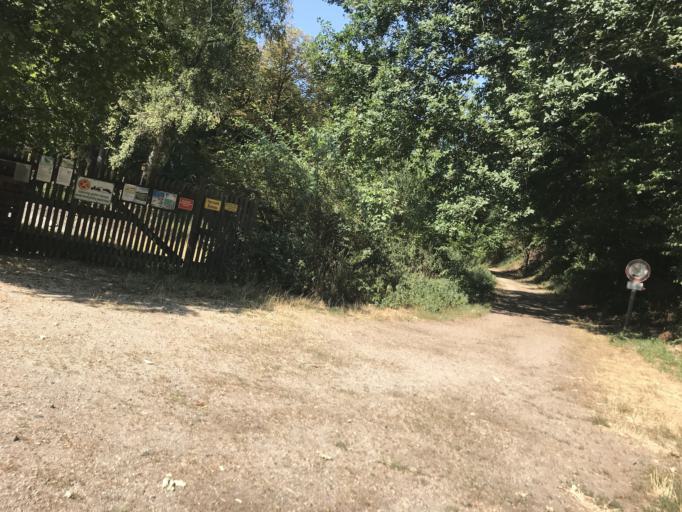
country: DE
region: Hesse
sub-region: Regierungsbezirk Darmstadt
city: Kiedrich
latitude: 50.0526
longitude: 8.0963
